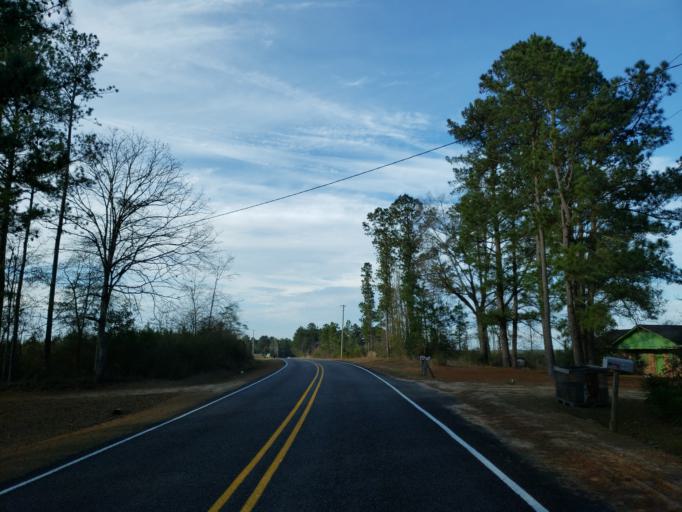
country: US
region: Mississippi
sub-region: Wayne County
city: Belmont
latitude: 31.4903
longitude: -88.5035
